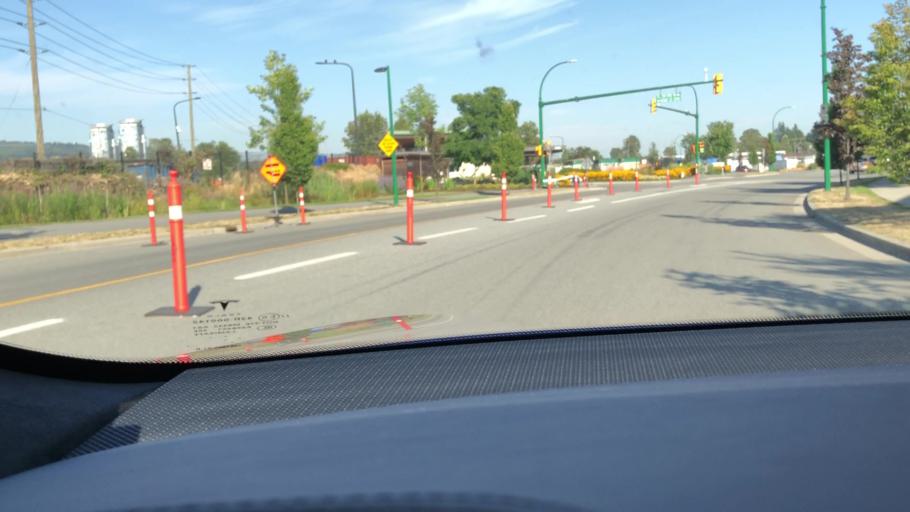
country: CA
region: British Columbia
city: Burnaby
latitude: 49.2617
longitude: -122.9973
